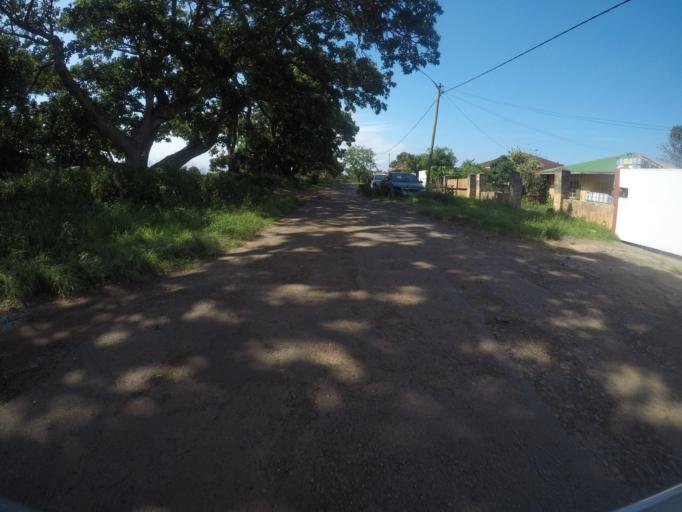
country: ZA
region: Eastern Cape
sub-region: Buffalo City Metropolitan Municipality
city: East London
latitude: -32.9696
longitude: 27.8750
